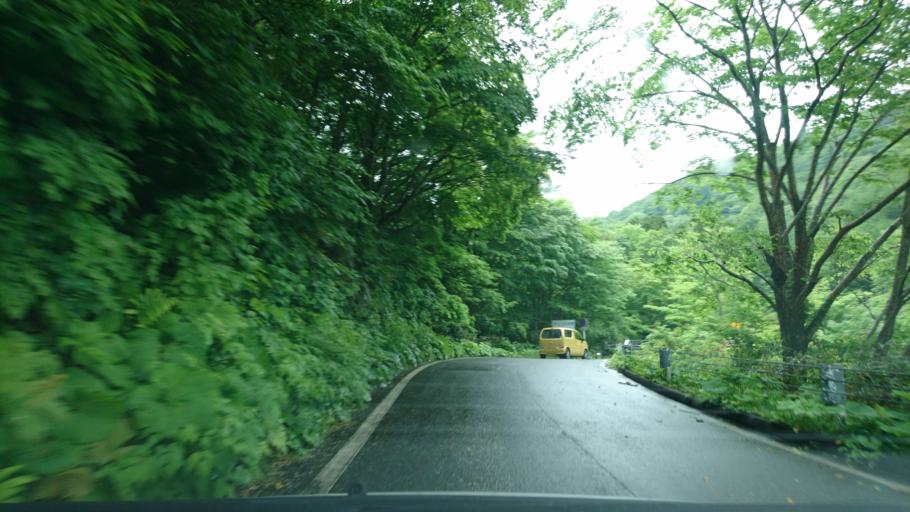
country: JP
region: Iwate
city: Ichinoseki
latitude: 38.9948
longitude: 140.8225
